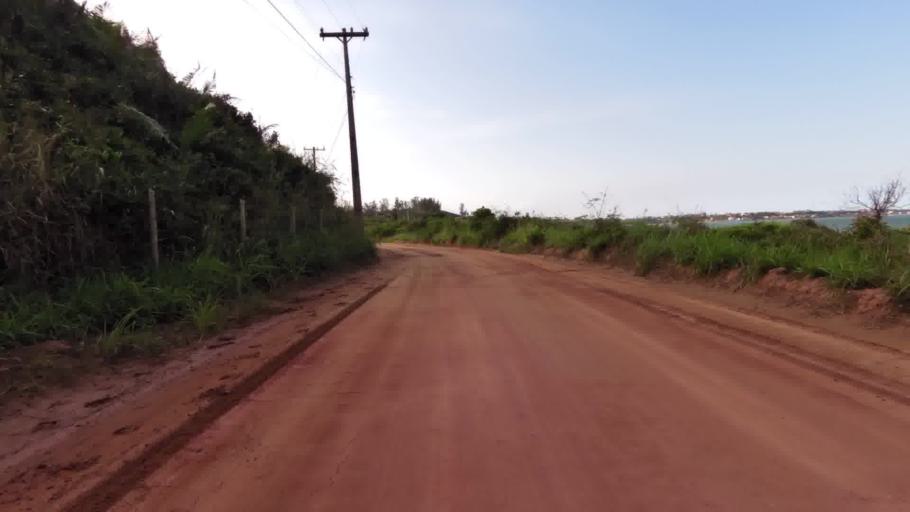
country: BR
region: Espirito Santo
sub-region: Piuma
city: Piuma
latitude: -20.8186
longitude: -40.6147
